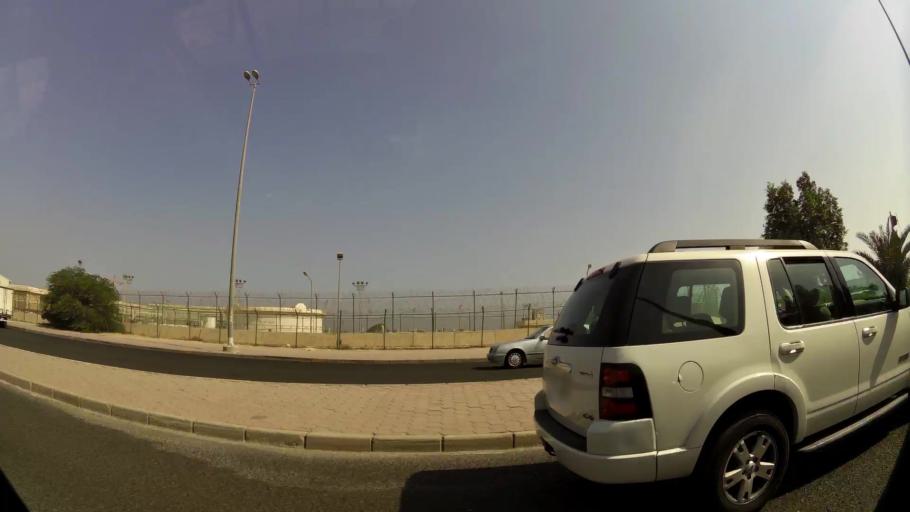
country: KW
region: Al Ahmadi
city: Al Manqaf
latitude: 29.1201
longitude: 48.1334
